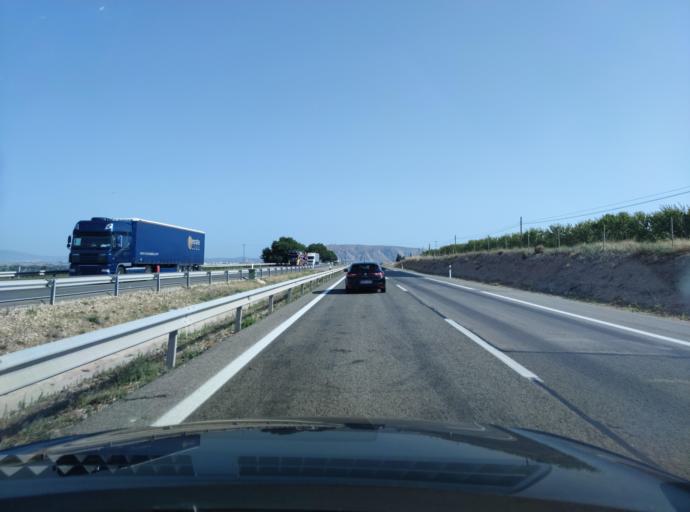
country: ES
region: Valencia
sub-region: Provincia de Alicante
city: Villena
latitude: 38.5864
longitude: -0.8436
